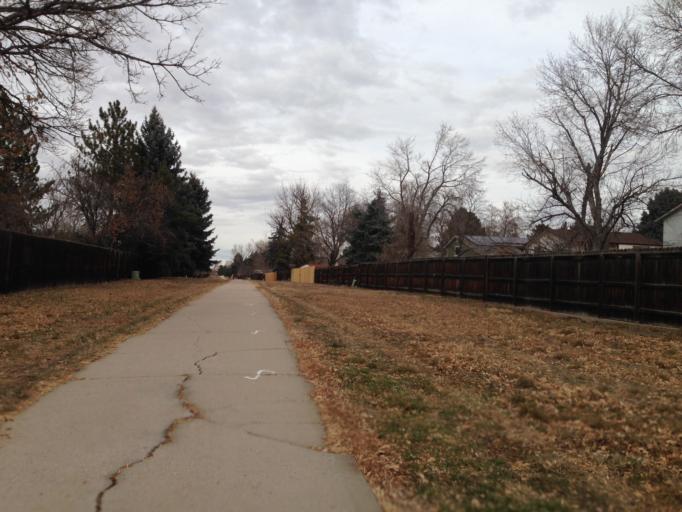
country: US
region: Colorado
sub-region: Adams County
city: Westminster
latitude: 39.8507
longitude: -105.0627
